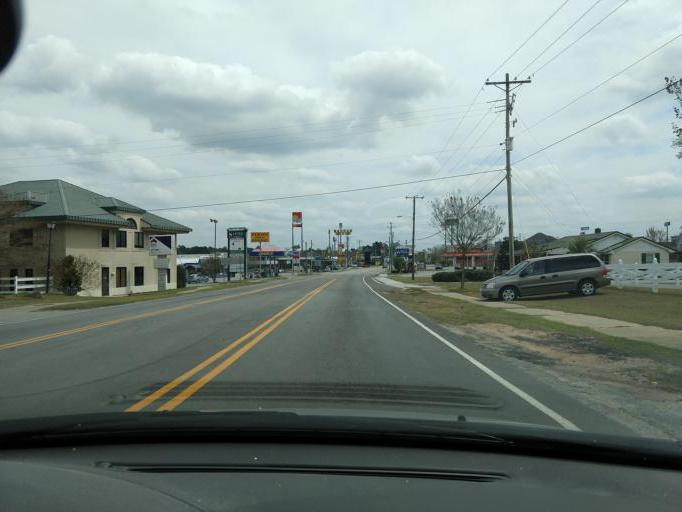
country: US
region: South Carolina
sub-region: Orangeburg County
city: Holly Hill
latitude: 33.4882
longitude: -80.4776
